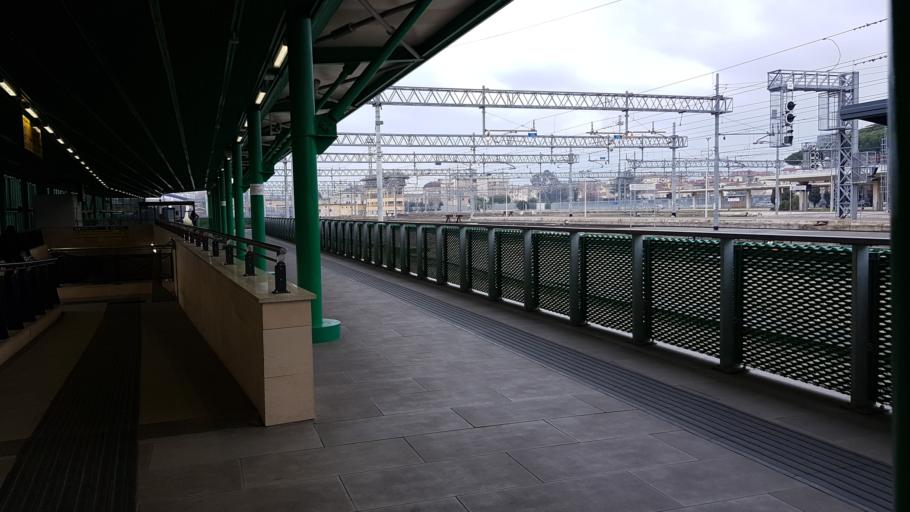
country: IT
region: Tuscany
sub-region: Province of Pisa
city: Pisa
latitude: 43.7077
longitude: 10.3974
